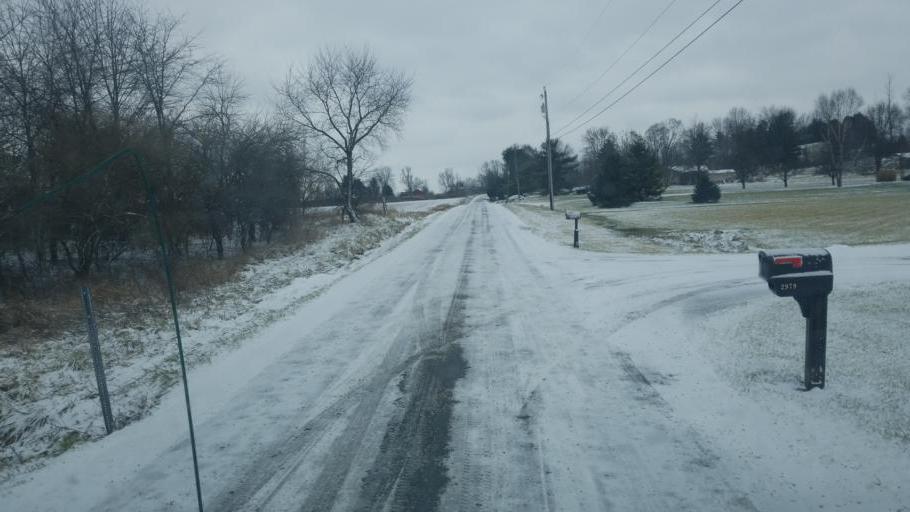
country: US
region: Ohio
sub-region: Delaware County
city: Sunbury
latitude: 40.2427
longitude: -82.7731
